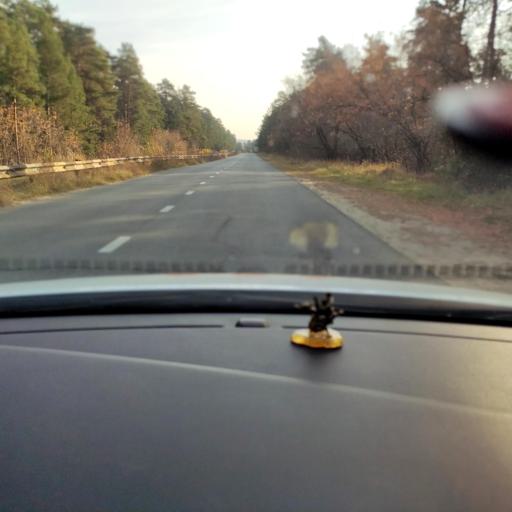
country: RU
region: Tatarstan
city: Osinovo
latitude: 55.8260
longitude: 48.9007
